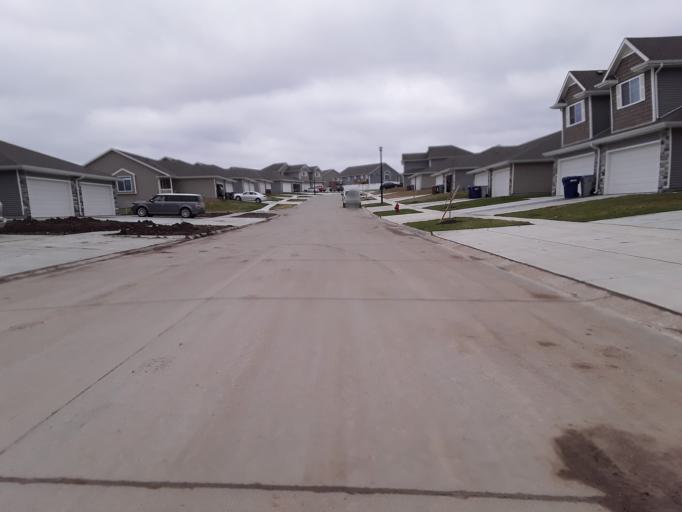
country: US
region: Nebraska
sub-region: Lancaster County
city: Lincoln
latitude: 40.8492
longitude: -96.5982
